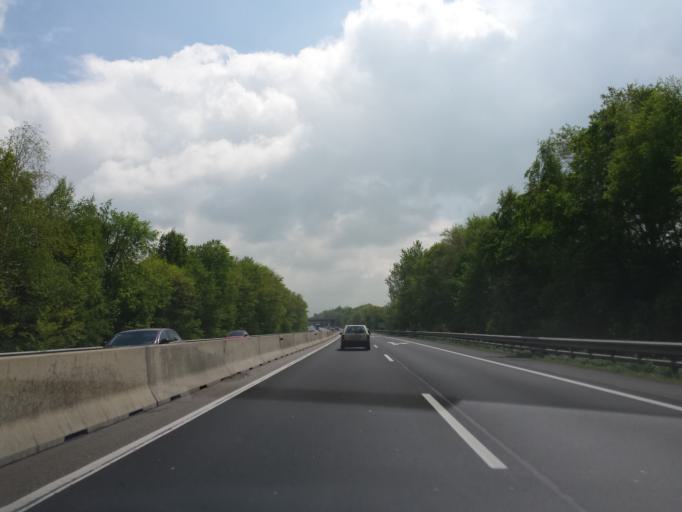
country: AT
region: Lower Austria
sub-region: Politischer Bezirk Bruck an der Leitha
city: Bruck an der Leitha
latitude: 48.0610
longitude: 16.7031
